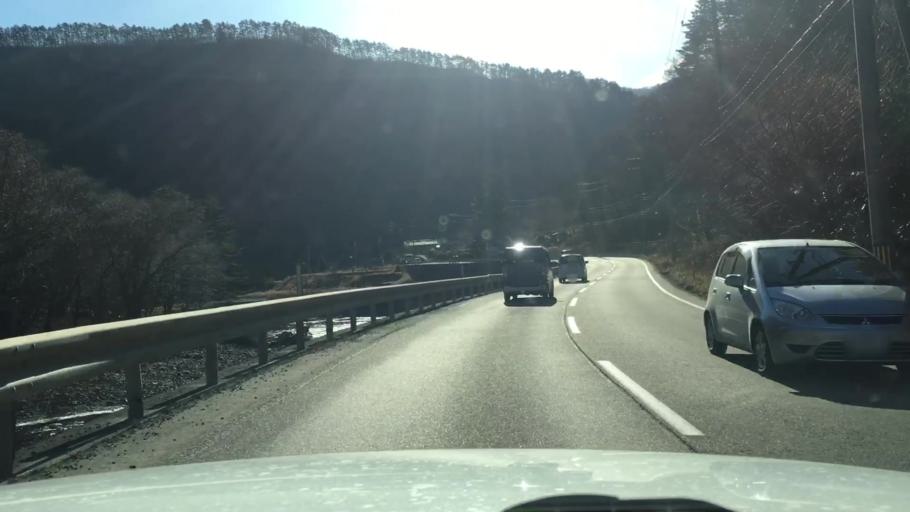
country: JP
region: Iwate
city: Miyako
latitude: 39.6096
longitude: 141.7880
